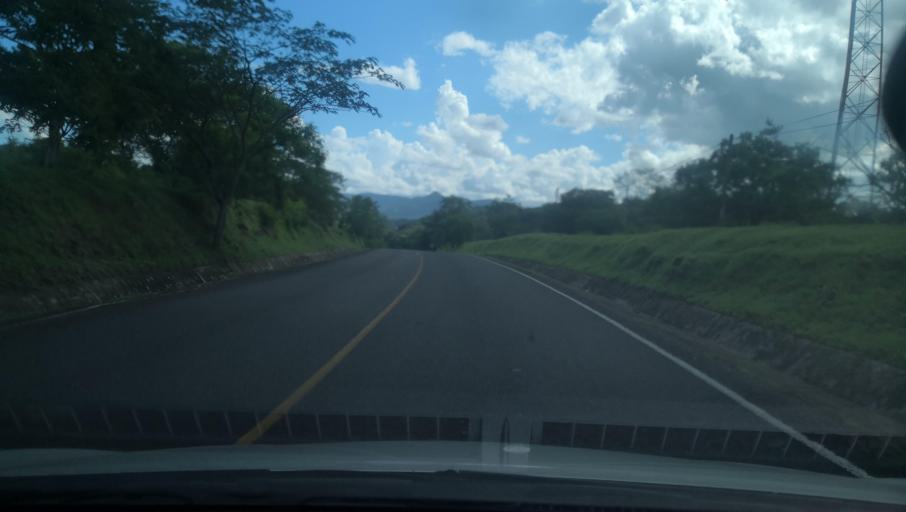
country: NI
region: Madriz
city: Somoto
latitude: 13.4670
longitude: -86.6536
